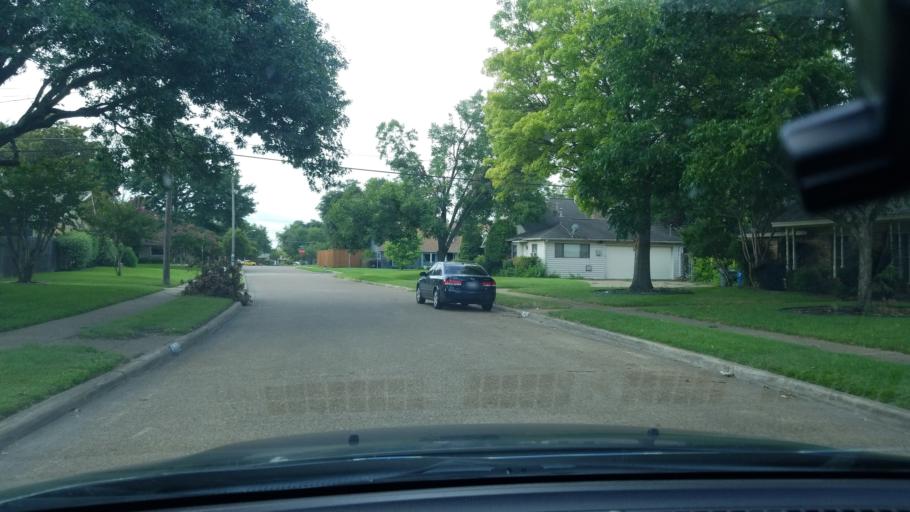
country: US
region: Texas
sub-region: Dallas County
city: Mesquite
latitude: 32.8197
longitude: -96.6865
